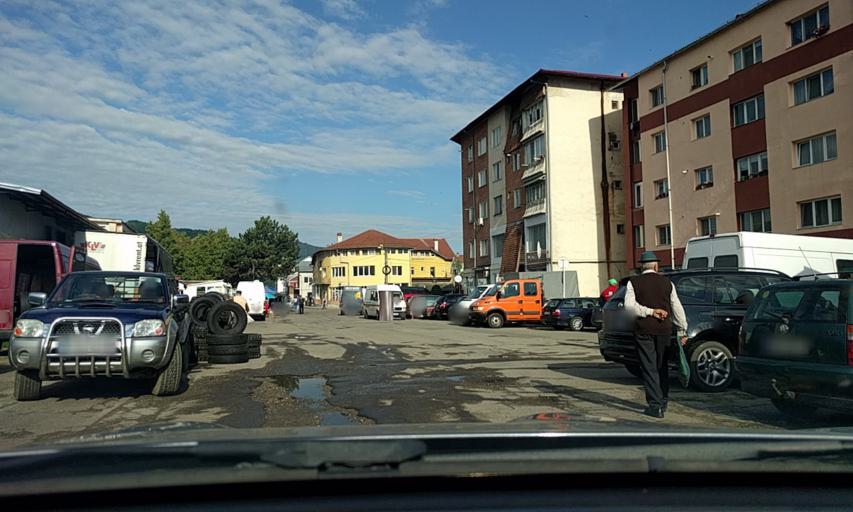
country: RO
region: Bistrita-Nasaud
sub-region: Oras Nasaud
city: Nasaud
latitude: 47.2815
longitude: 24.4127
